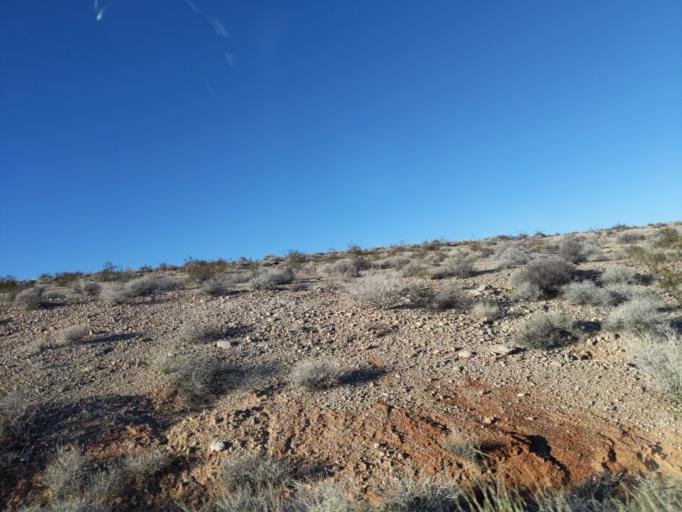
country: US
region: Nevada
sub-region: Clark County
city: Moapa Valley
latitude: 36.4177
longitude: -114.6001
